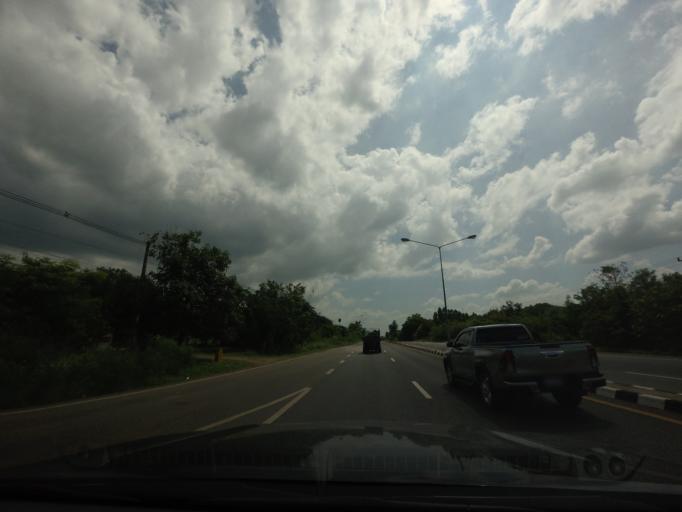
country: TH
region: Phetchabun
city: Phetchabun
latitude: 16.2129
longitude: 101.0890
